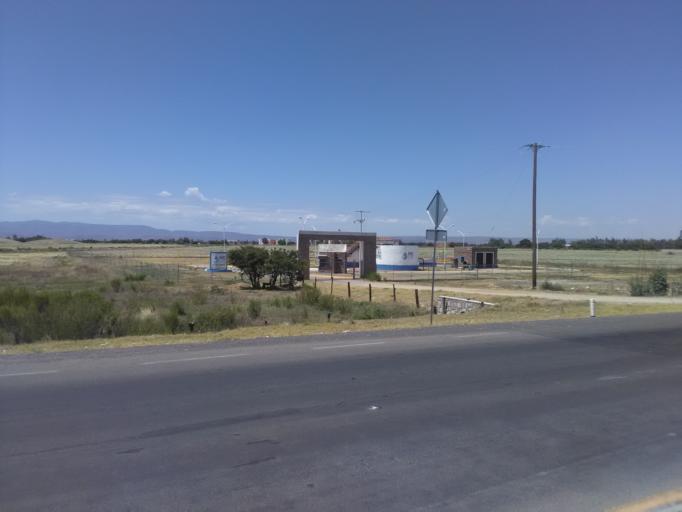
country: MX
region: Durango
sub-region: Durango
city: Jose Refugio Salcido
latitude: 24.0227
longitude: -104.5402
